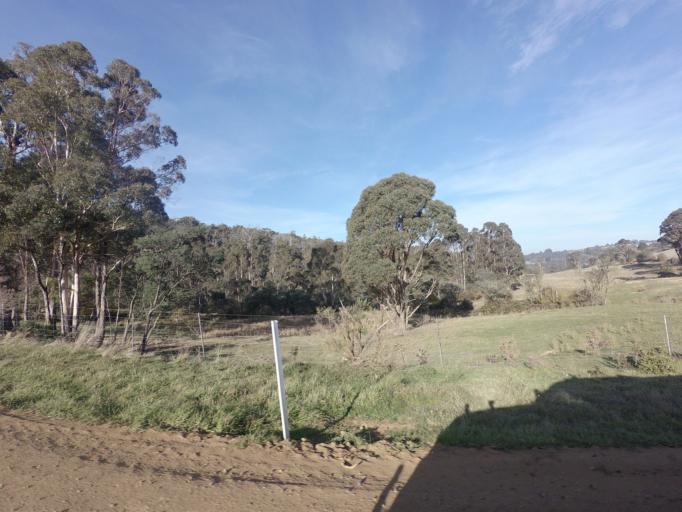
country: AU
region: Tasmania
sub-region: Brighton
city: Bridgewater
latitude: -42.4666
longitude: 147.3781
